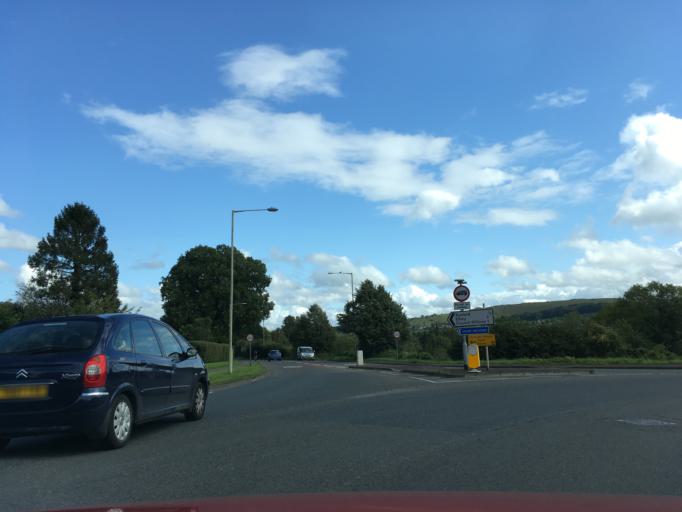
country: GB
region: England
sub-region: Gloucestershire
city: Stonehouse
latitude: 51.7416
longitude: -2.2767
